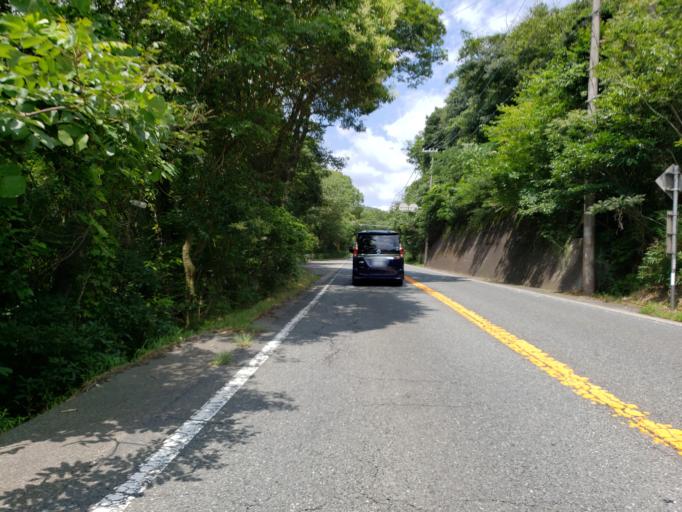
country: JP
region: Hyogo
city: Aioi
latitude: 34.7822
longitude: 134.4375
